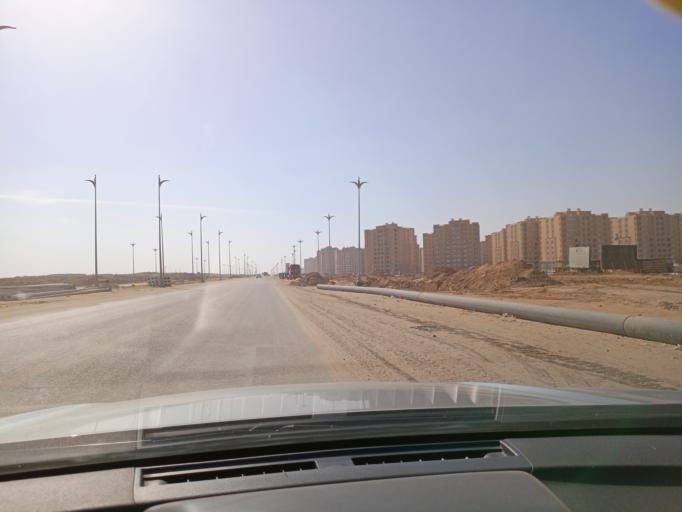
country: EG
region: Muhafazat al Qalyubiyah
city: Al Khankah
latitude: 30.0230
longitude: 31.6643
